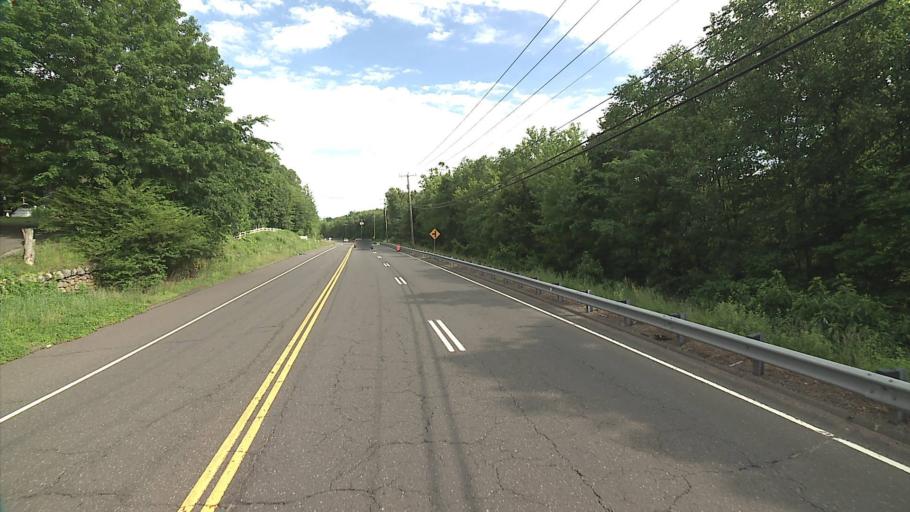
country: US
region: Connecticut
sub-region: New Haven County
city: Naugatuck
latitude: 41.5073
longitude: -73.0600
